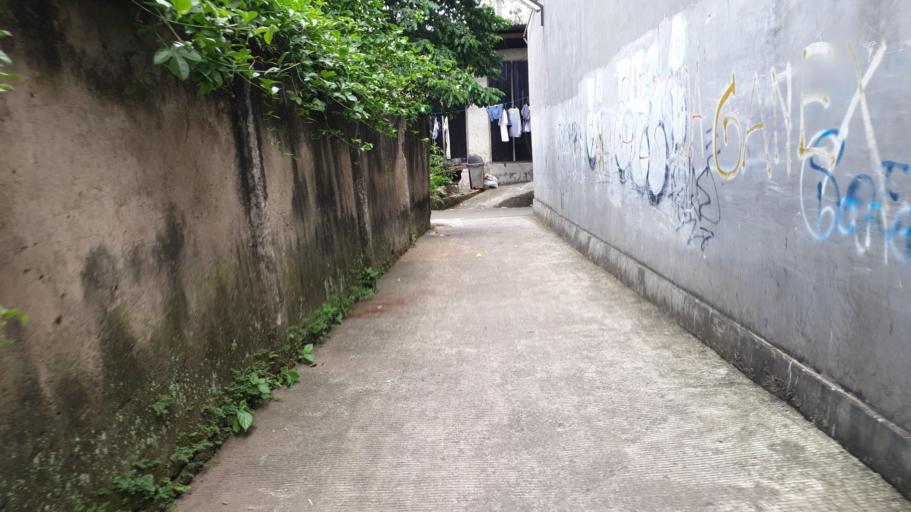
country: ID
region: Jakarta Raya
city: Jakarta
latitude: -6.2654
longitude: 106.7912
